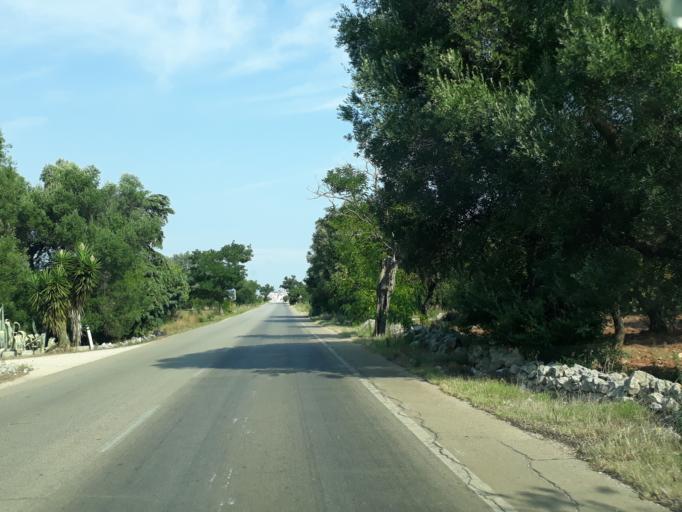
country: IT
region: Apulia
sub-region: Provincia di Brindisi
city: Carovigno
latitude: 40.6889
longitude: 17.6756
